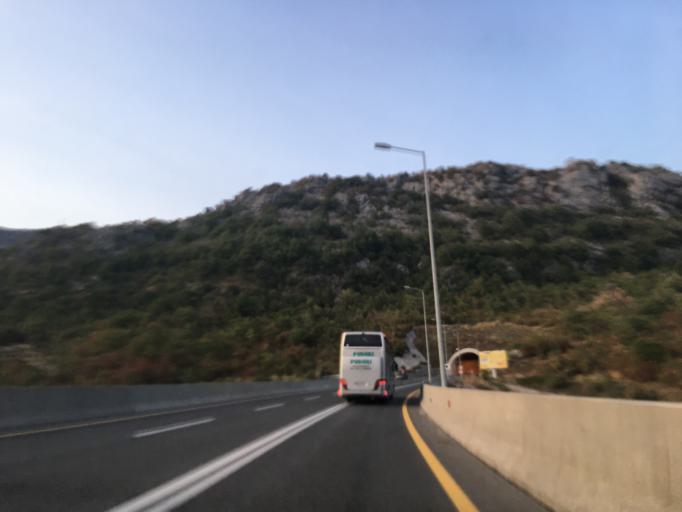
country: ME
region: Bar
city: Sutomore
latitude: 42.2253
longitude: 19.0517
